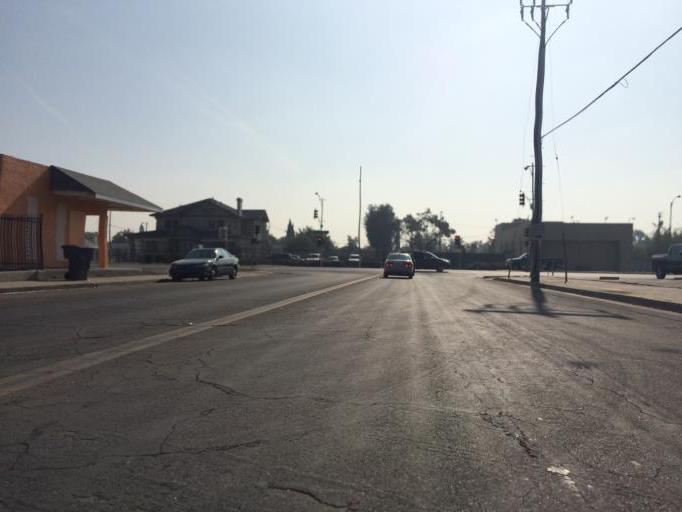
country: US
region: California
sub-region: Fresno County
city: Fresno
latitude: 36.7364
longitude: -119.7644
